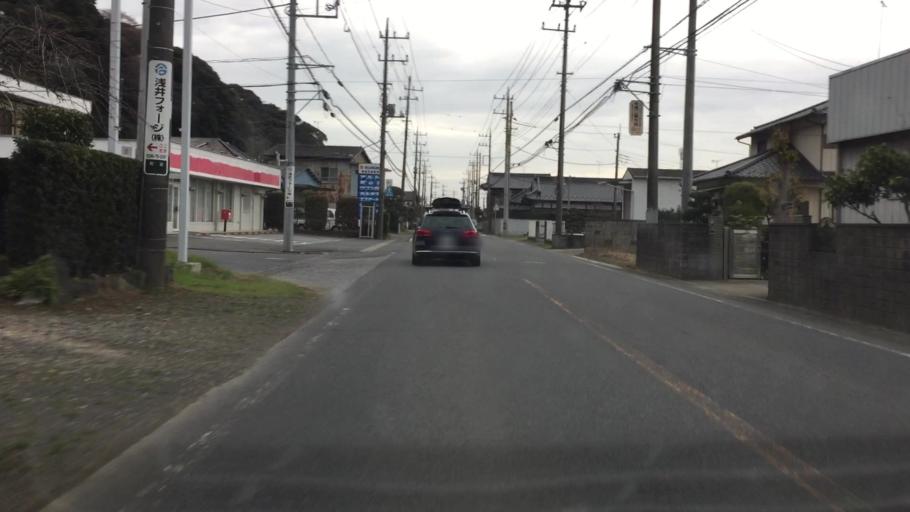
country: JP
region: Ibaraki
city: Inashiki
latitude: 35.9303
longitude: 140.3551
